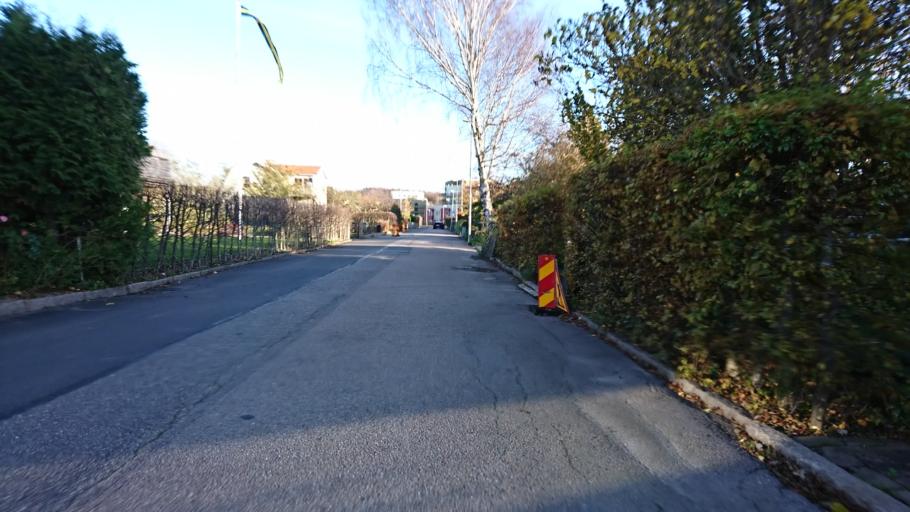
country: SE
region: Vaestra Goetaland
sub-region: Molndal
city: Moelndal
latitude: 57.6534
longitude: 11.9976
